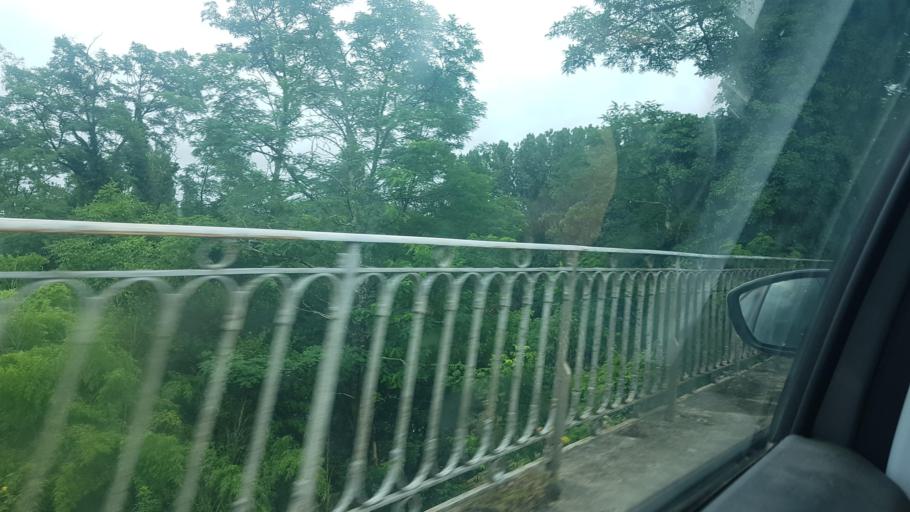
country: FR
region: Aquitaine
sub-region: Departement du Lot-et-Garonne
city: Montayral
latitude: 44.4949
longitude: 1.0824
